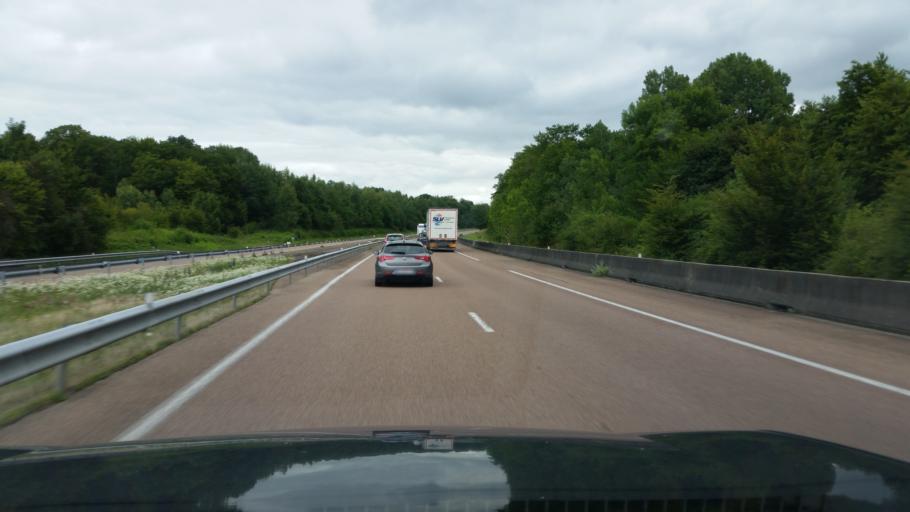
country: FR
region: Franche-Comte
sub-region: Departement du Jura
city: Bletterans
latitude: 46.7093
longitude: 5.4828
